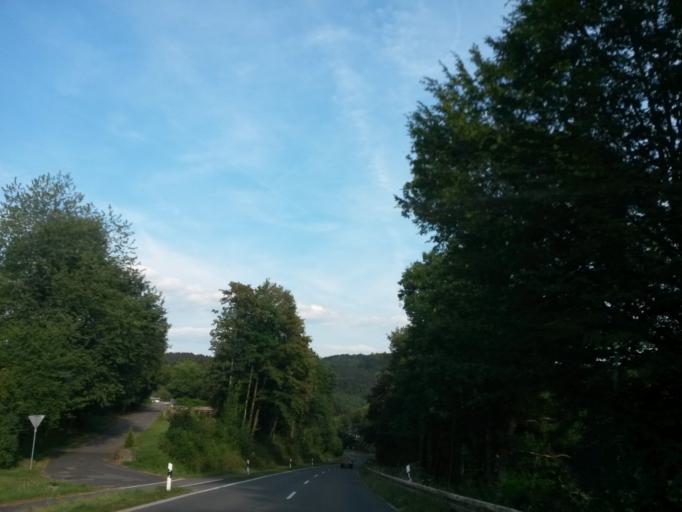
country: DE
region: North Rhine-Westphalia
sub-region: Regierungsbezirk Koln
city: Lindlar
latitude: 51.0384
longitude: 7.4231
